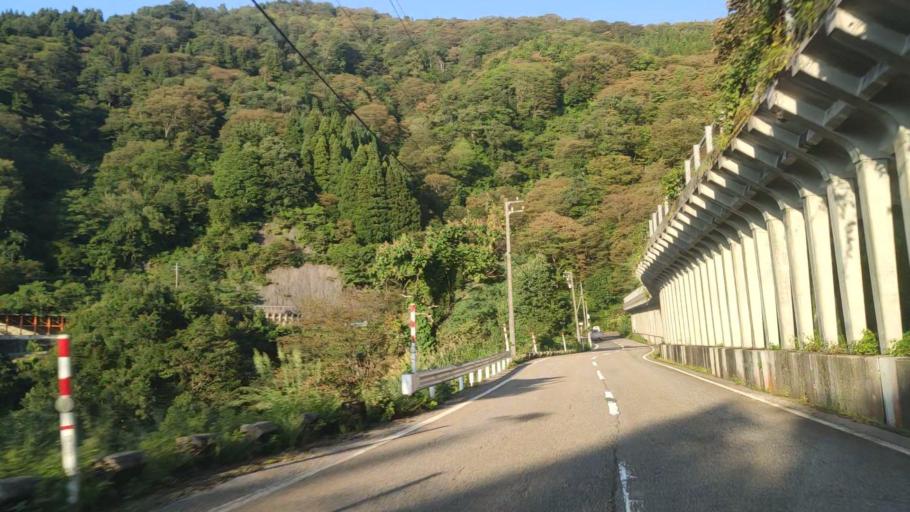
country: JP
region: Toyama
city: Yatsuomachi-higashikumisaka
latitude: 36.5177
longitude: 137.0289
